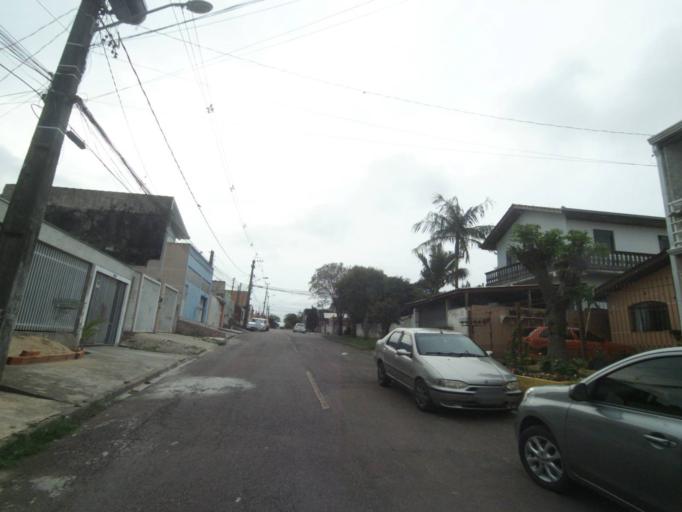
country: BR
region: Parana
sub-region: Sao Jose Dos Pinhais
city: Sao Jose dos Pinhais
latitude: -25.5524
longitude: -49.2610
